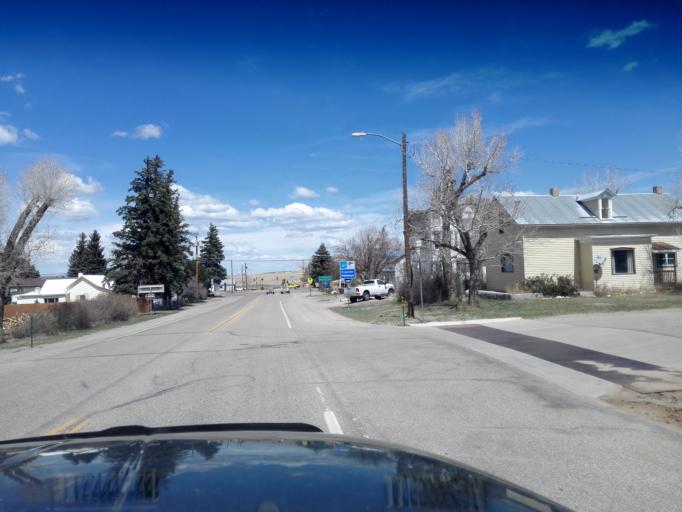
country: US
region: Colorado
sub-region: Custer County
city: Westcliffe
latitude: 38.1346
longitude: -105.4638
